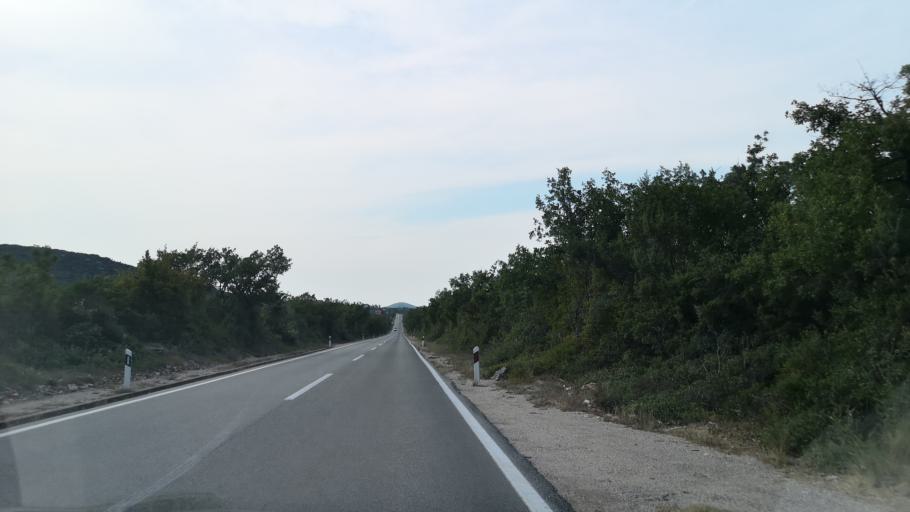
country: HR
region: Sibensko-Kniniska
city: Zaton
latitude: 43.8457
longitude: 15.7710
